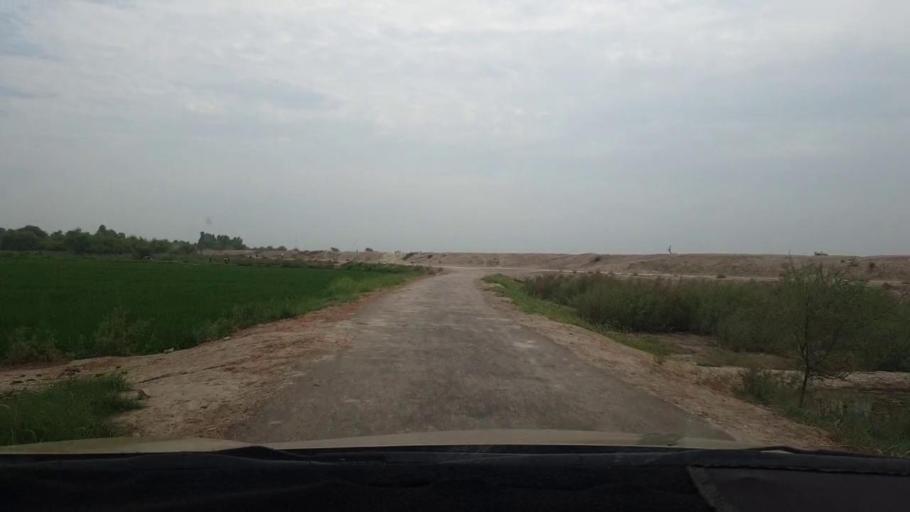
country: PK
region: Sindh
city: Naudero
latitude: 27.6213
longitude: 68.3324
